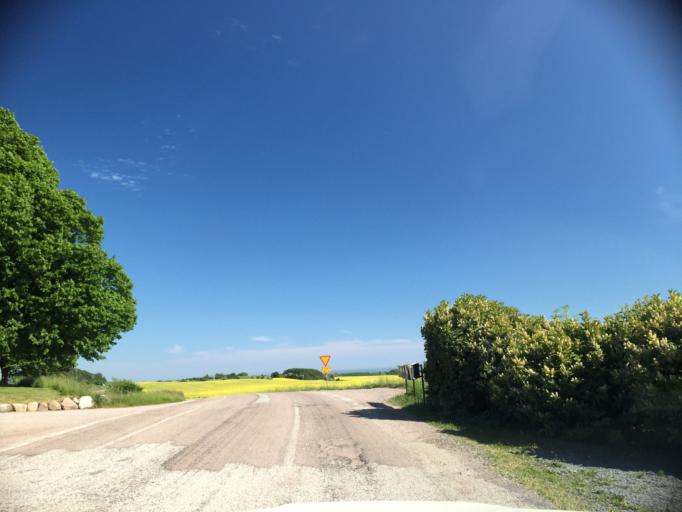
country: SE
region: Skane
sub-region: Ystads Kommun
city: Ystad
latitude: 55.4498
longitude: 13.7614
